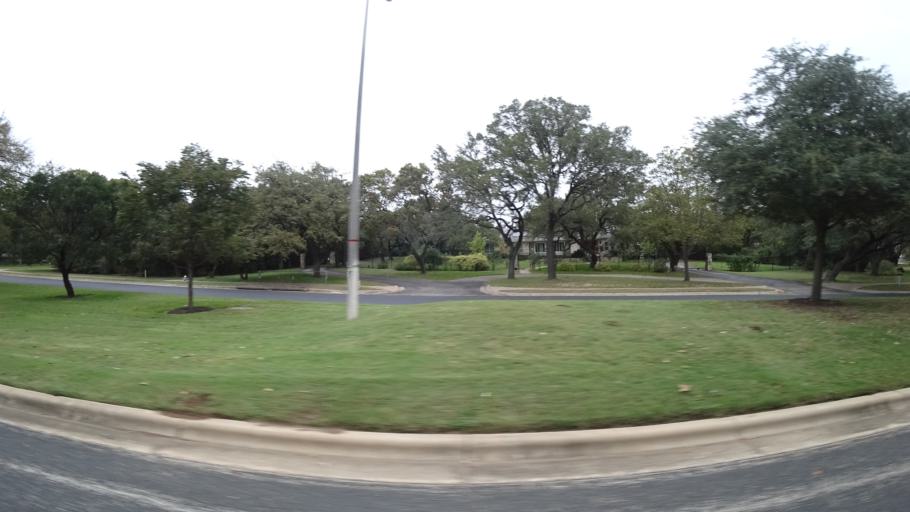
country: US
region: Texas
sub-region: Williamson County
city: Anderson Mill
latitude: 30.4413
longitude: -97.8285
